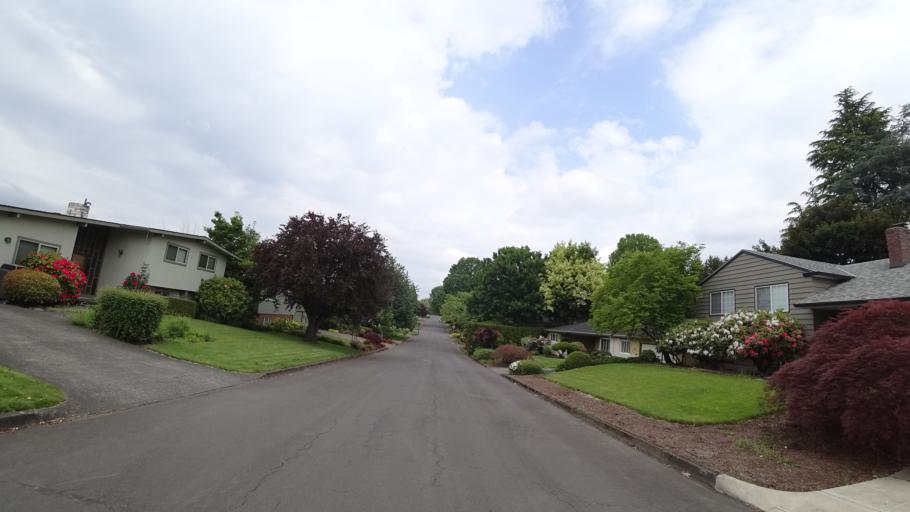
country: US
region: Oregon
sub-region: Clackamas County
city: Milwaukie
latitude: 45.4858
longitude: -122.6267
